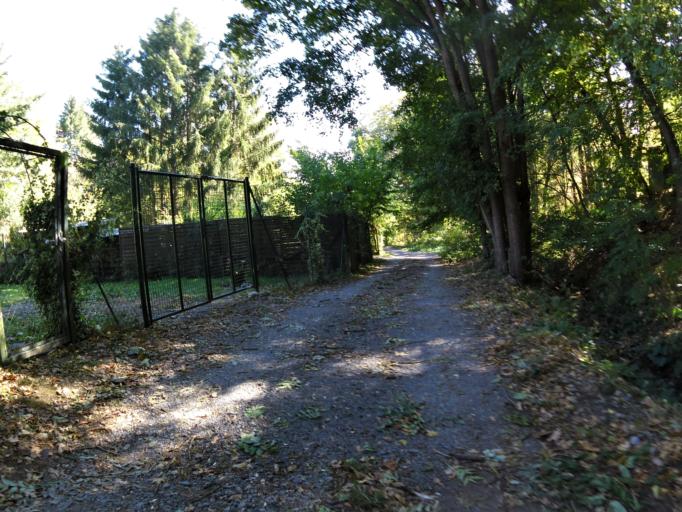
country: DE
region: Bavaria
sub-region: Regierungsbezirk Unterfranken
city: Reichenberg
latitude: 49.7539
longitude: 9.9308
